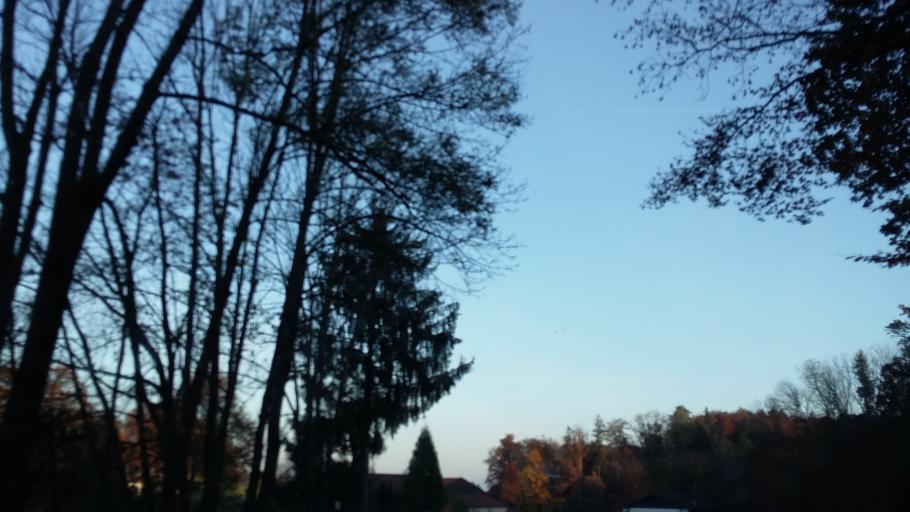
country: DE
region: Bavaria
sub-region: Upper Bavaria
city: Rimsting
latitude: 47.8906
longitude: 12.3484
